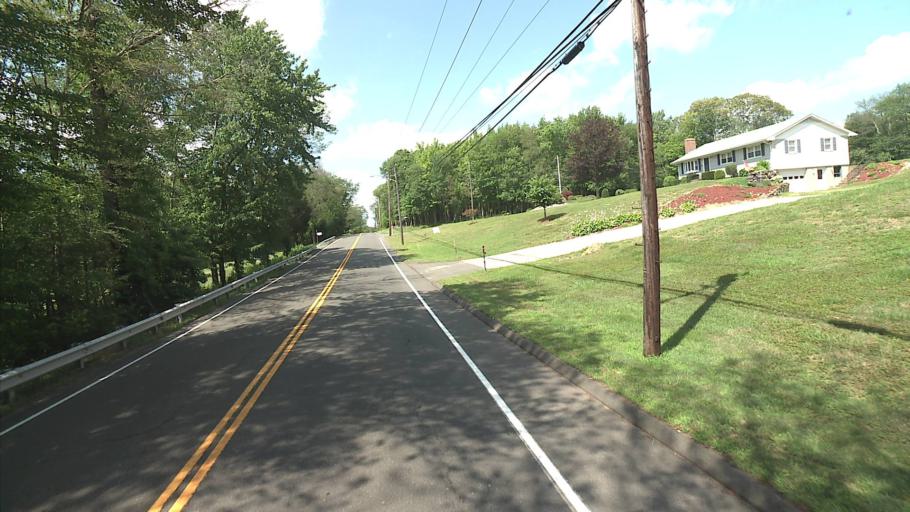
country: US
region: Connecticut
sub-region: Middlesex County
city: Higganum
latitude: 41.4422
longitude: -72.5559
